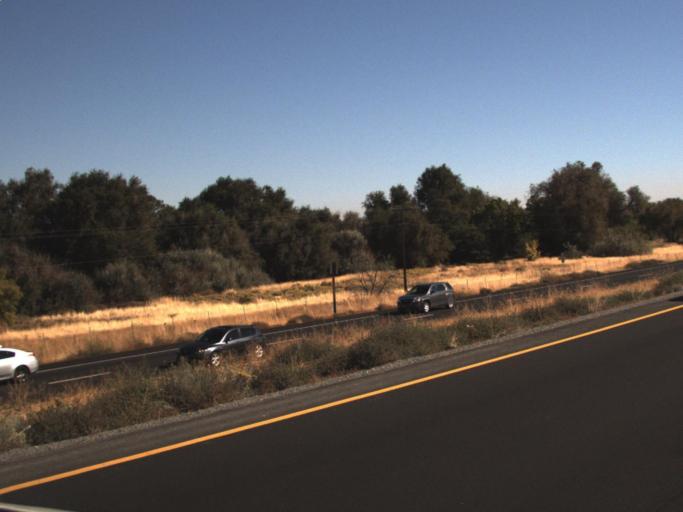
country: US
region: Washington
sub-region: Franklin County
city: West Pasco
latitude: 46.2267
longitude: -119.1815
